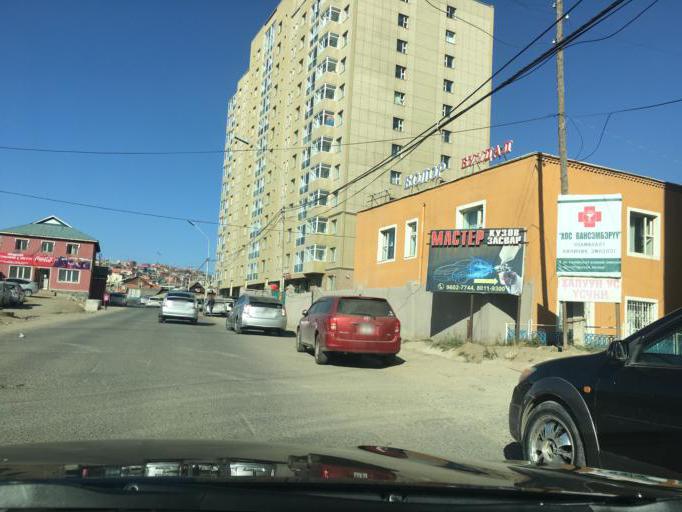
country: MN
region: Ulaanbaatar
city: Ulaanbaatar
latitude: 47.9277
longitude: 106.8771
